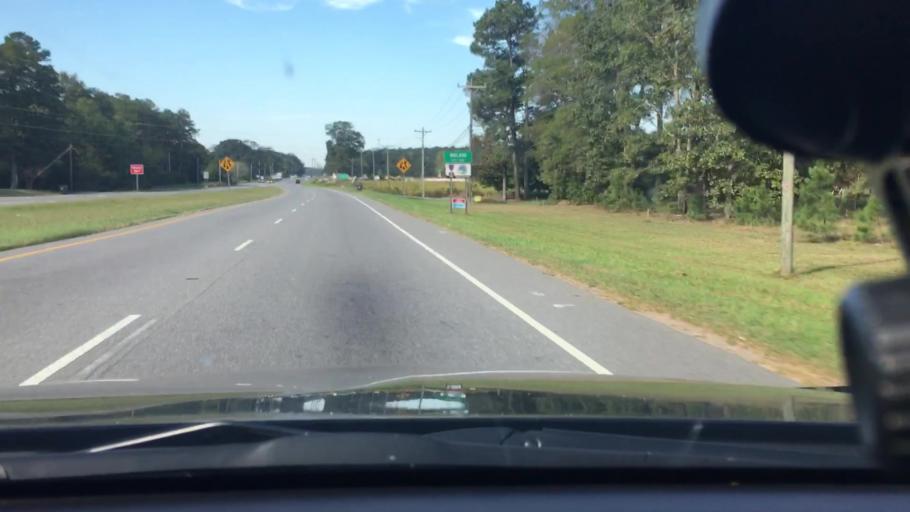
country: US
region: North Carolina
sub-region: Cabarrus County
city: Midland
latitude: 35.2548
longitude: -80.4835
